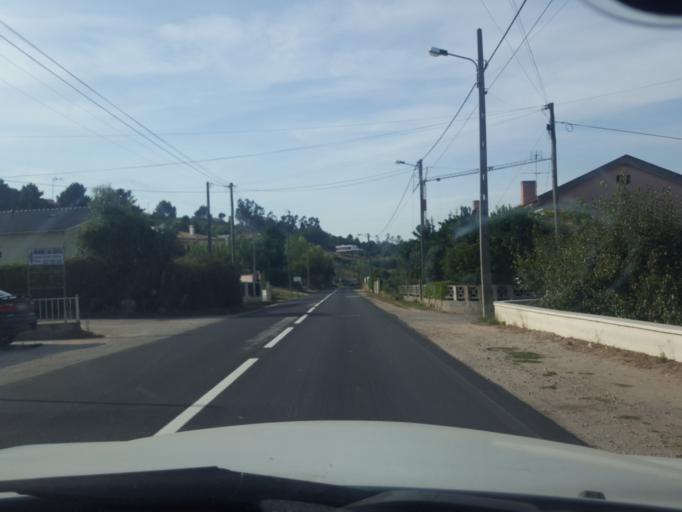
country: PT
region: Leiria
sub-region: Leiria
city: Leiria
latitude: 39.7013
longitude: -8.7902
